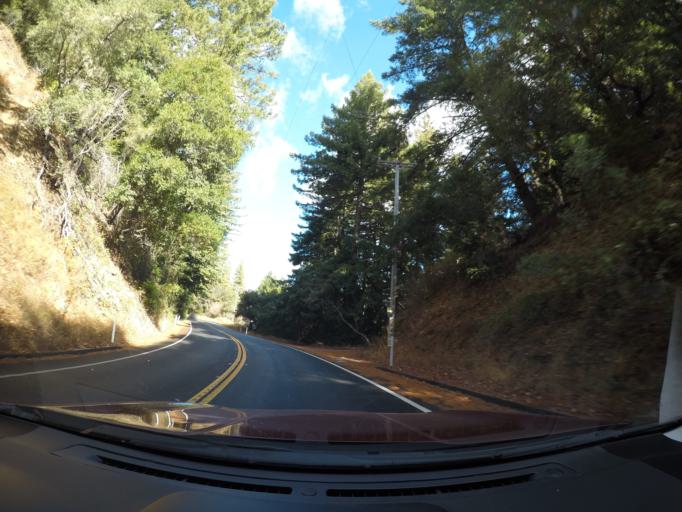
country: US
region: California
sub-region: Santa Cruz County
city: Boulder Creek
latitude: 37.2244
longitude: -122.1472
